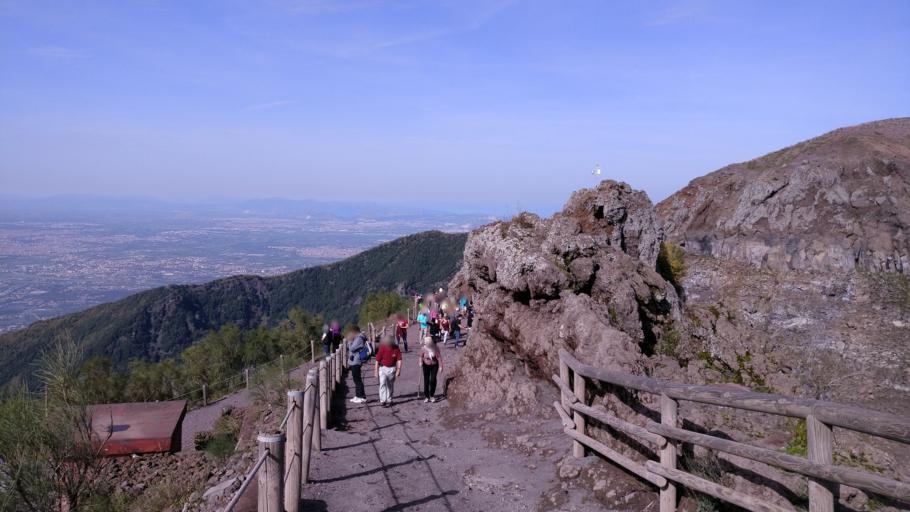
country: IT
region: Campania
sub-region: Provincia di Napoli
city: Torre del Greco
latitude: 40.8213
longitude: 14.4227
